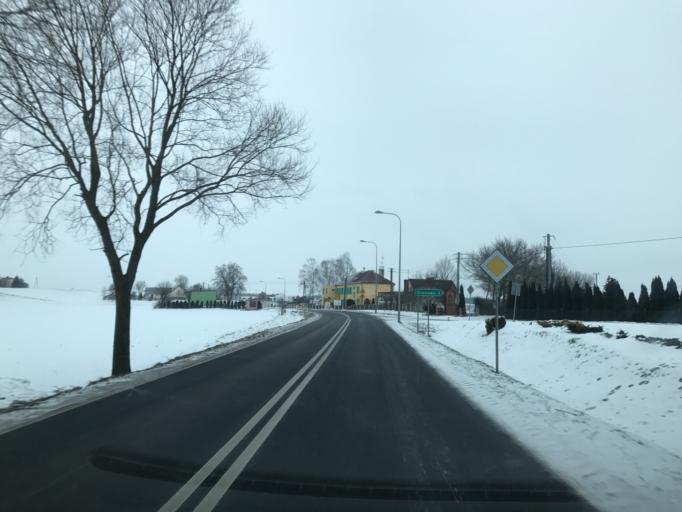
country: PL
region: Warmian-Masurian Voivodeship
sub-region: Powiat dzialdowski
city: Rybno
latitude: 53.3836
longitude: 19.8152
